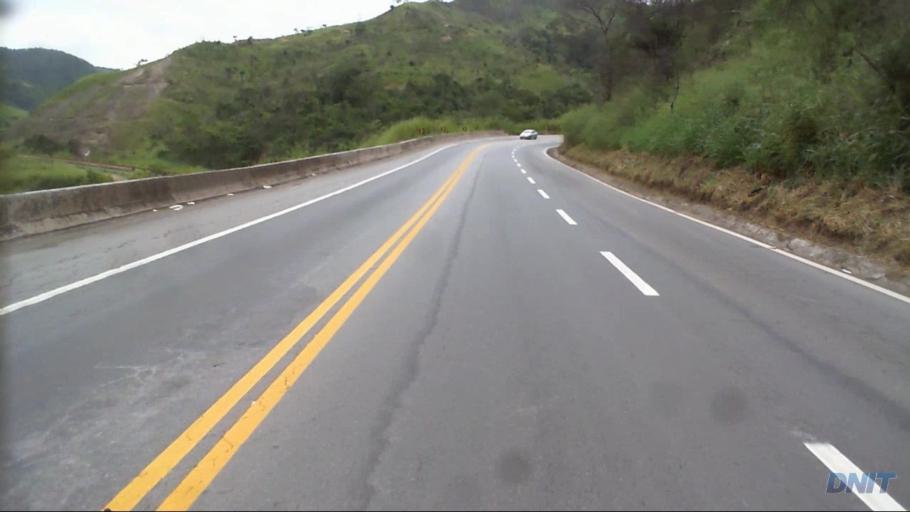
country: BR
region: Minas Gerais
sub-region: Timoteo
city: Timoteo
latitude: -19.6396
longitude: -42.8162
